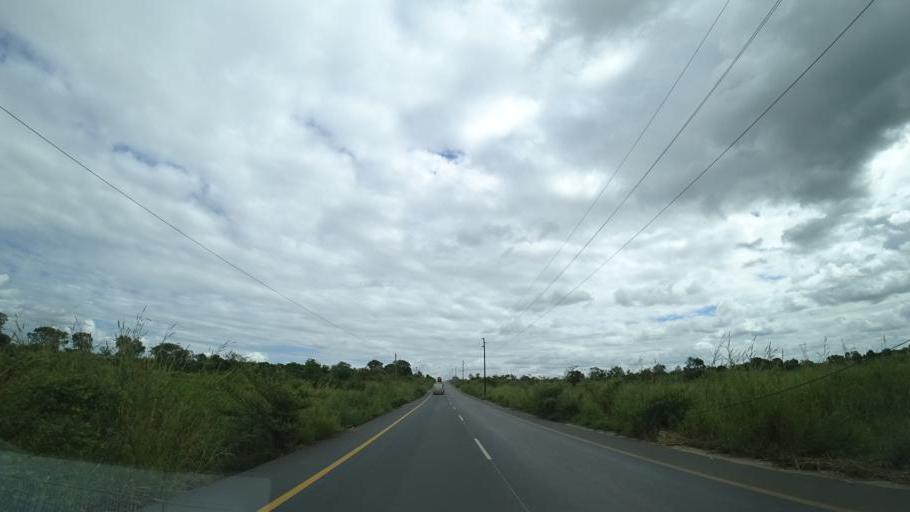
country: MZ
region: Sofala
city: Dondo
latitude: -19.5068
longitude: 34.6065
